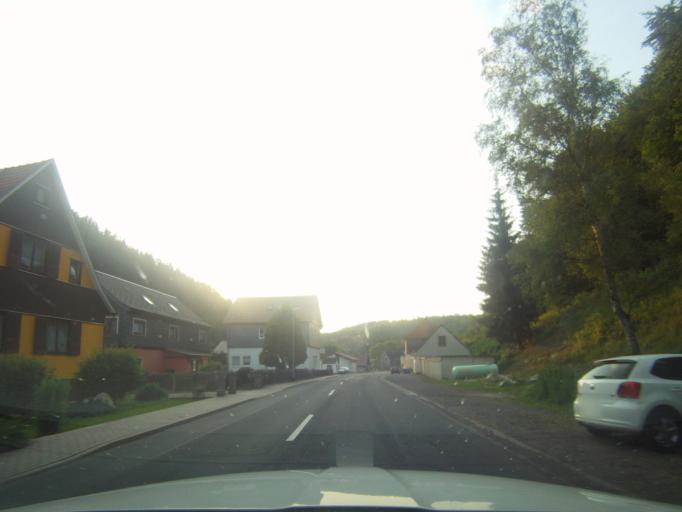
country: DE
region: Thuringia
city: Frauenwald
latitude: 50.5022
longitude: 10.8459
